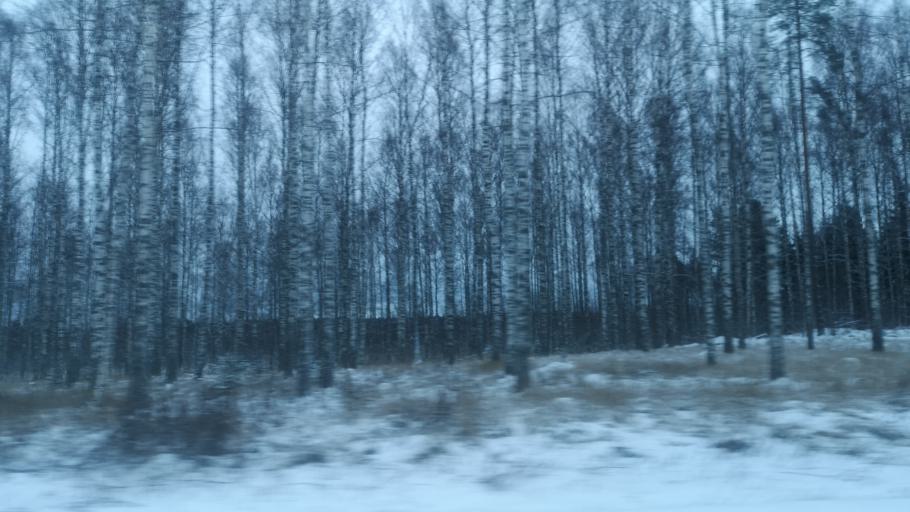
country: FI
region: Southern Savonia
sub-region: Savonlinna
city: Enonkoski
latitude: 62.0820
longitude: 28.6993
